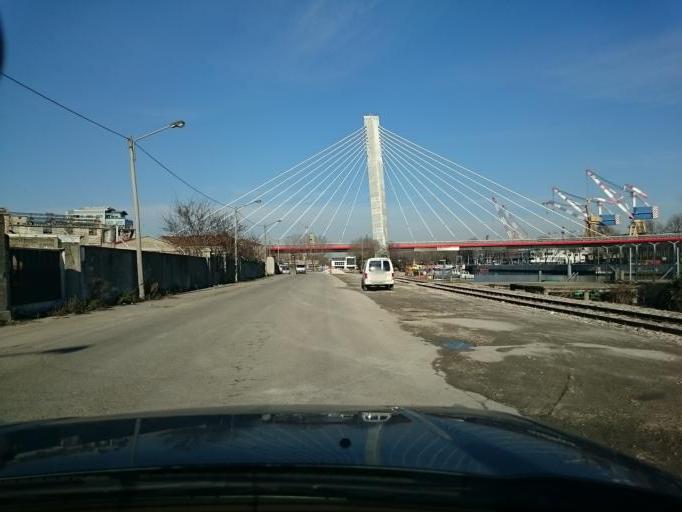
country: IT
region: Veneto
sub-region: Provincia di Venezia
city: Mestre
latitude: 45.4710
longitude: 12.2358
